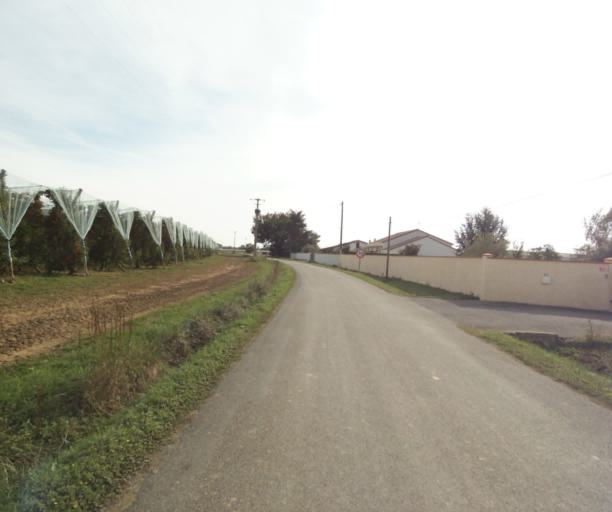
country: FR
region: Midi-Pyrenees
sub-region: Departement du Tarn-et-Garonne
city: Bressols
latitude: 43.9409
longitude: 1.3377
